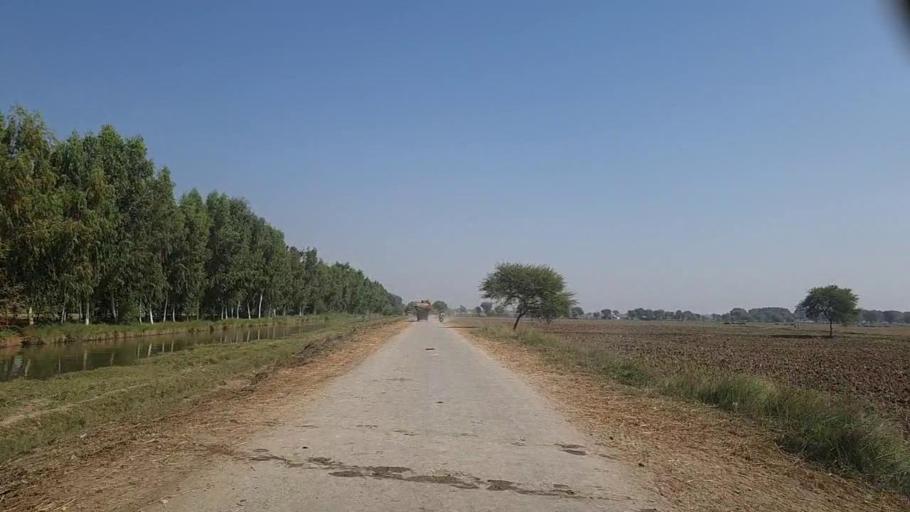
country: PK
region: Sindh
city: Thul
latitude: 28.2395
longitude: 68.7941
